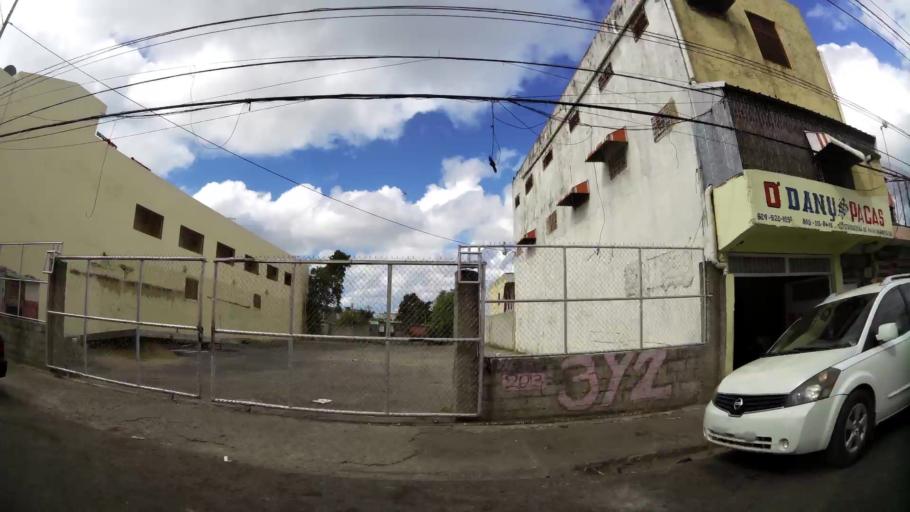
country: DO
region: Nacional
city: San Carlos
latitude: 18.4817
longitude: -69.8920
